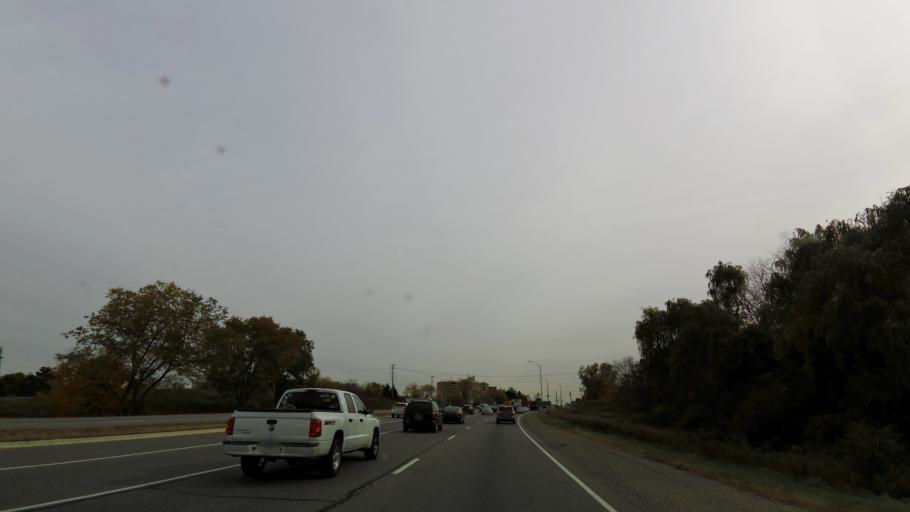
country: CA
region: Ontario
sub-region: Wellington County
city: Guelph
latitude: 43.5147
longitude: -80.2443
